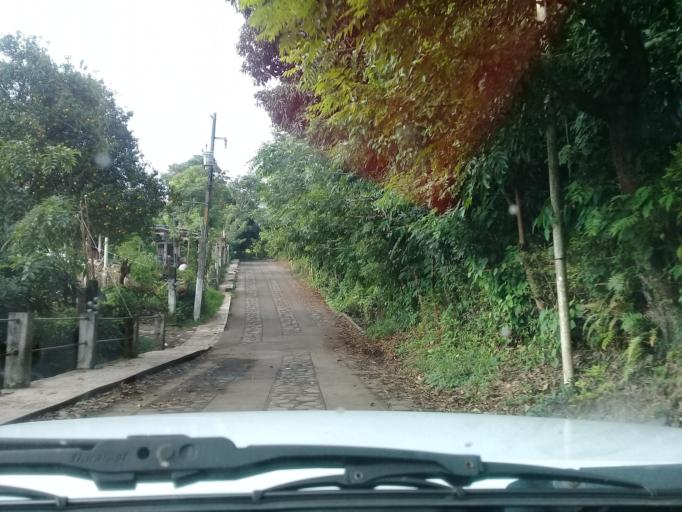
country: MX
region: Veracruz
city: Catemaco
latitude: 18.4294
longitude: -95.1255
